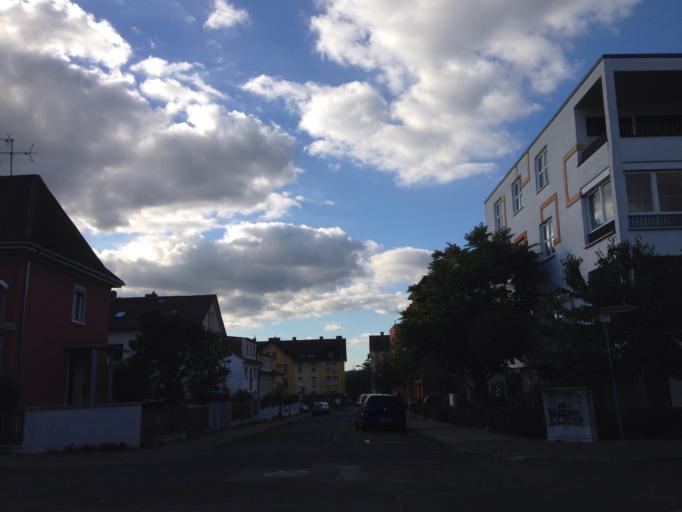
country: DE
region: Hesse
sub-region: Regierungsbezirk Giessen
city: Giessen
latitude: 50.5711
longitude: 8.6591
